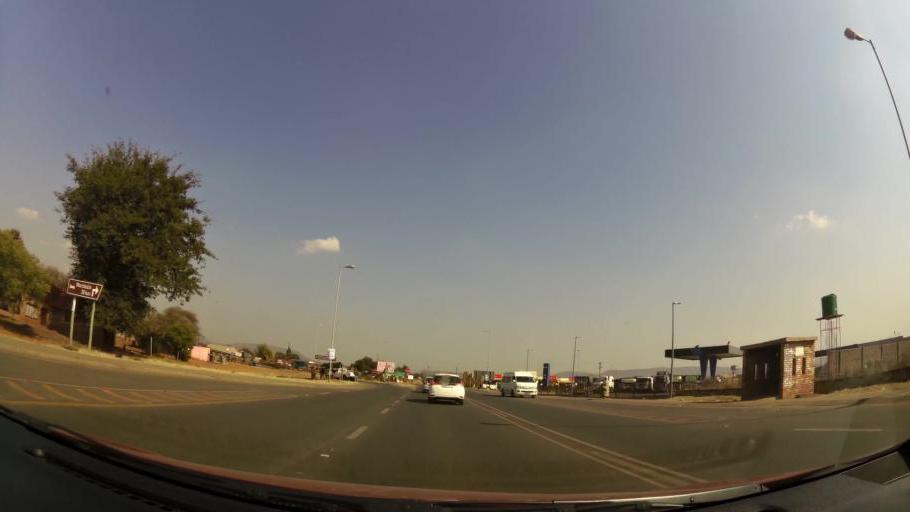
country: ZA
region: North-West
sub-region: Bojanala Platinum District Municipality
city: Mogwase
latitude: -25.3771
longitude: 27.0617
